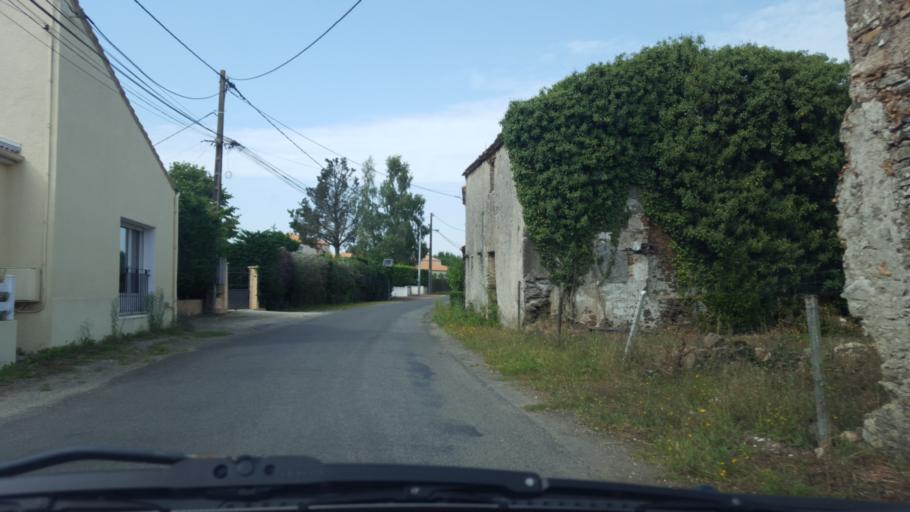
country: FR
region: Pays de la Loire
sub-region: Departement de la Loire-Atlantique
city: Saint-Philbert-de-Grand-Lieu
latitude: 47.0018
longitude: -1.6325
